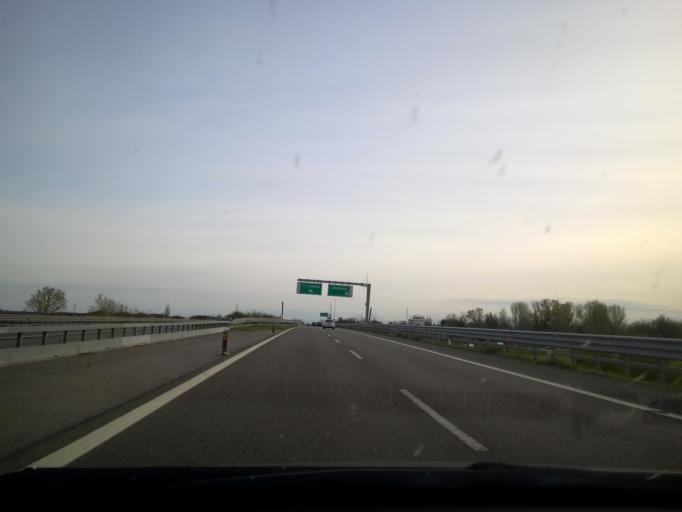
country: IT
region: Lombardy
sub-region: Provincia di Cremona
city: San Felice
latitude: 45.1460
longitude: 10.0727
